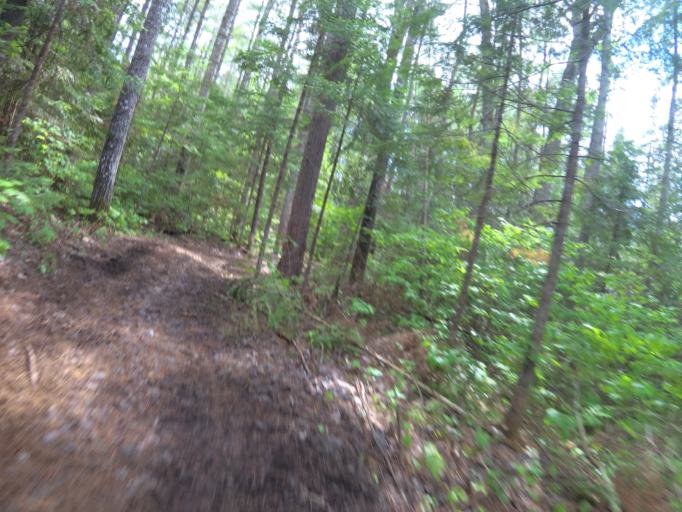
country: CA
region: Ontario
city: Renfrew
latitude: 45.1222
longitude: -76.8453
